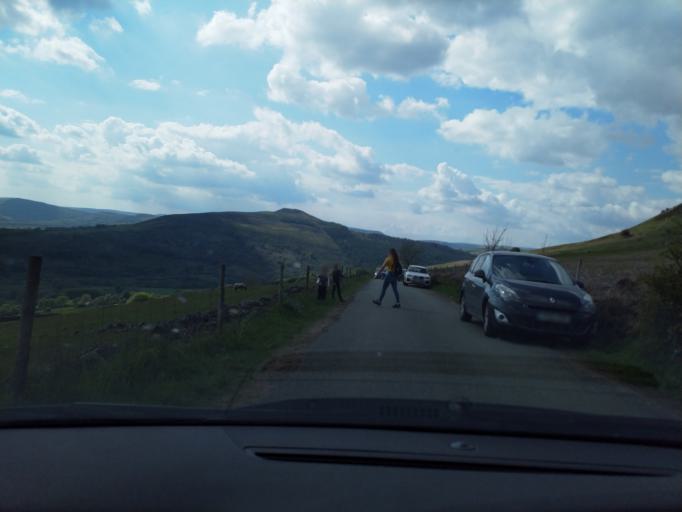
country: GB
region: England
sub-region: Derbyshire
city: Hathersage
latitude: 53.3529
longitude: -1.6819
